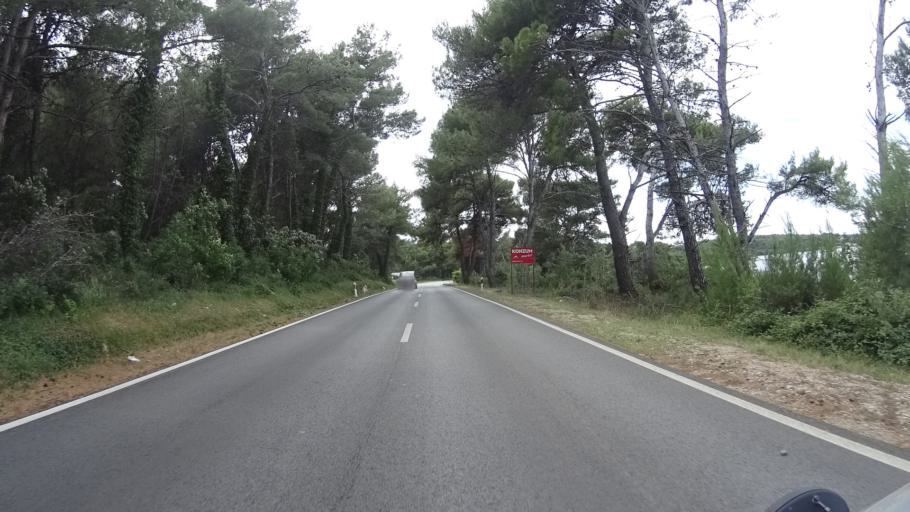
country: HR
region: Istarska
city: Medulin
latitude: 44.8165
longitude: 13.8902
